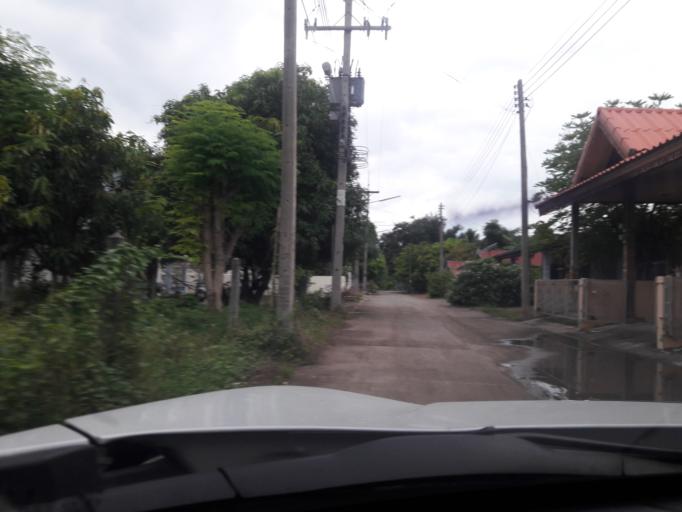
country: TH
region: Lop Buri
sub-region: Amphoe Tha Luang
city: Tha Luang
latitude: 15.0669
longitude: 101.1059
